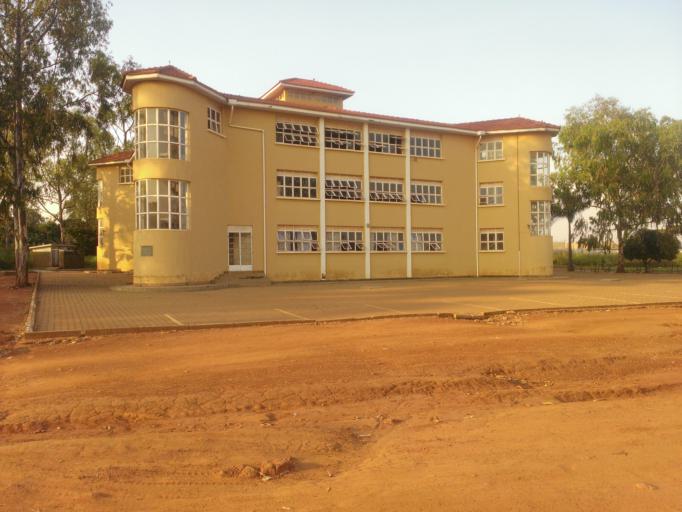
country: UG
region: Northern Region
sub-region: Gulu District
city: Gulu
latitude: 2.7798
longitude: 32.3064
